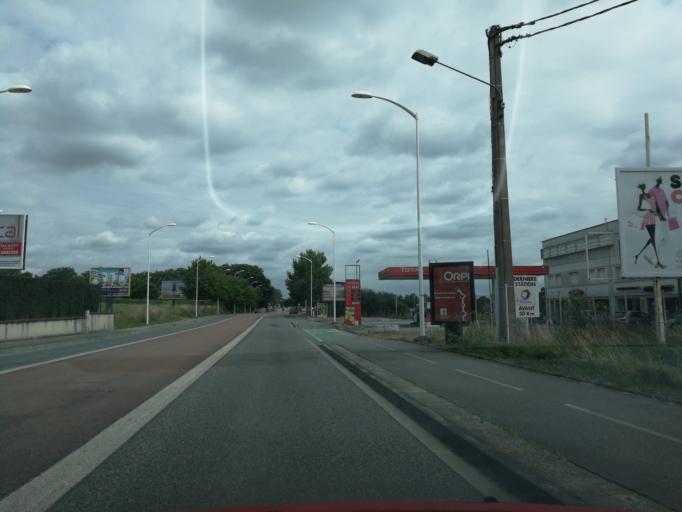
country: FR
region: Midi-Pyrenees
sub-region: Departement de la Haute-Garonne
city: Balma
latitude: 43.5897
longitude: 1.5136
